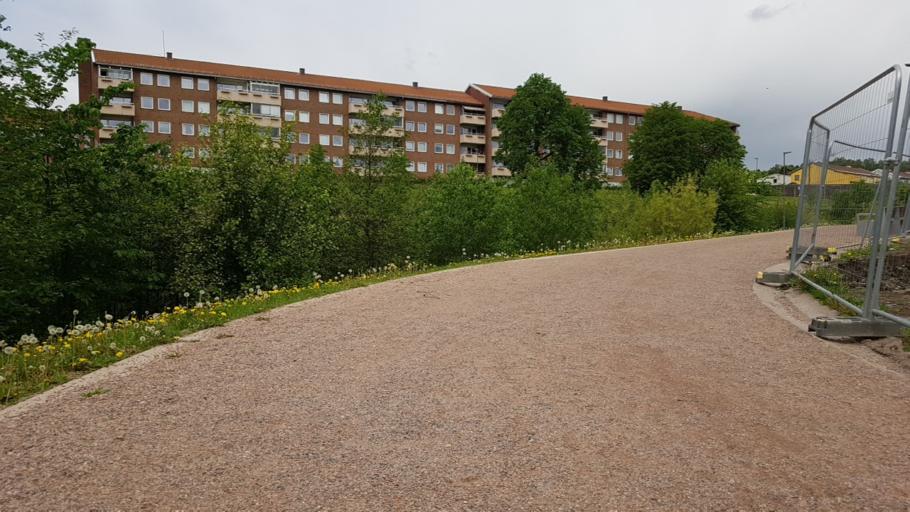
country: NO
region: Oslo
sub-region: Oslo
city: Oslo
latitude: 59.9391
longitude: 10.8217
